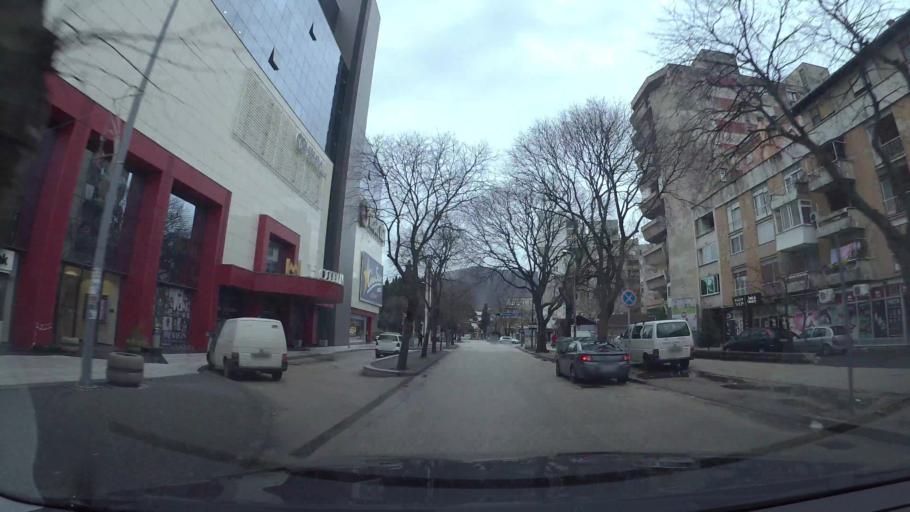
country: BA
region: Federation of Bosnia and Herzegovina
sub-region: Hercegovacko-Bosanski Kanton
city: Mostar
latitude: 43.3486
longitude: 17.8046
